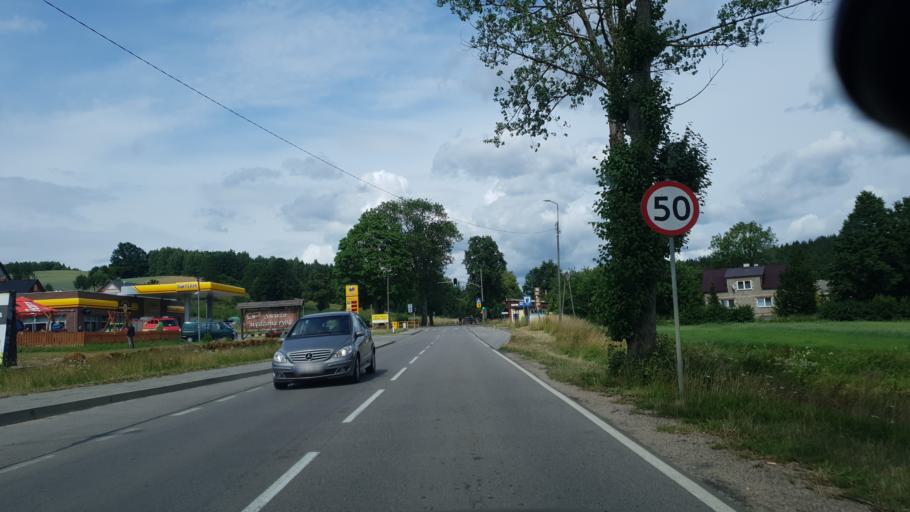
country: PL
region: Pomeranian Voivodeship
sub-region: Powiat kartuski
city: Chmielno
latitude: 54.3038
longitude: 18.1469
